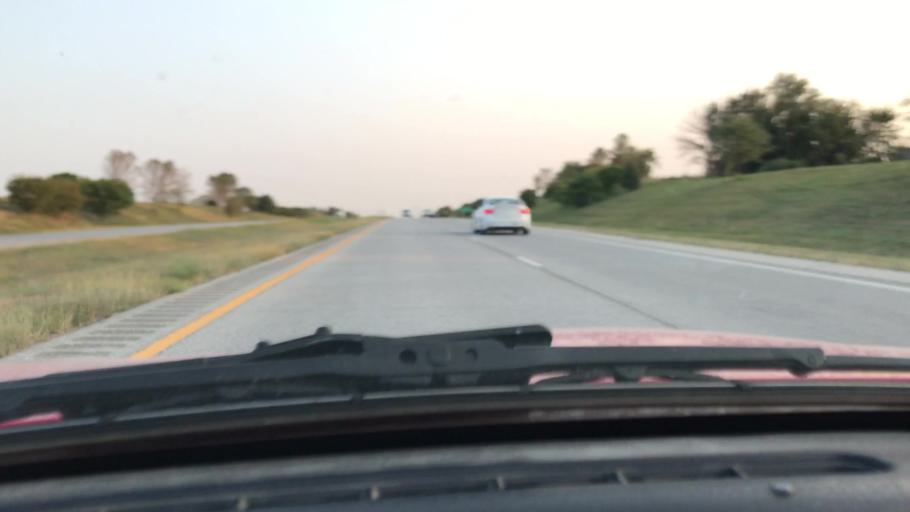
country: US
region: Nebraska
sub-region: Lancaster County
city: Lincoln
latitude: 40.7769
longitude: -96.7274
